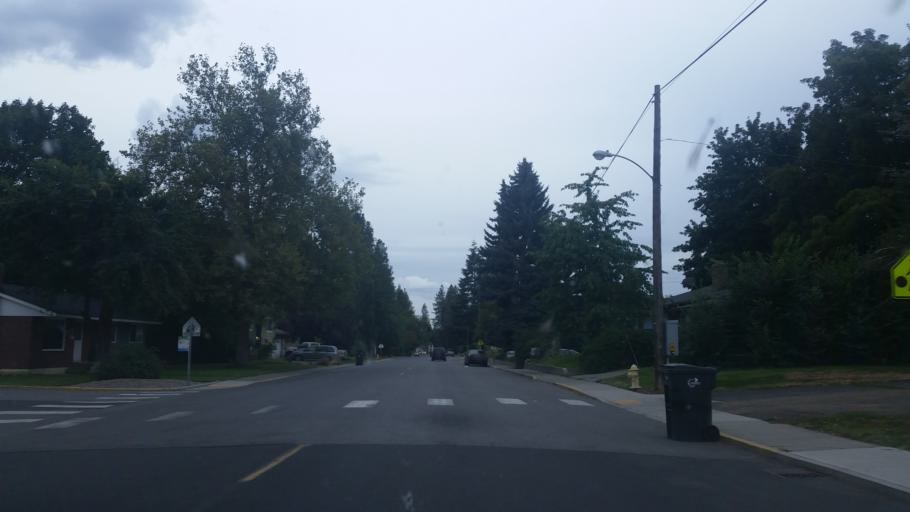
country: US
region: Washington
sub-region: Spokane County
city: Cheney
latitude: 47.4957
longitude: -117.5756
